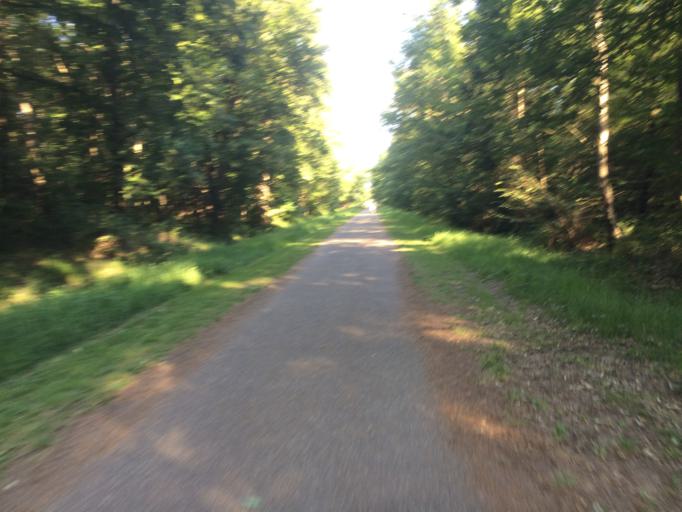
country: FR
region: Ile-de-France
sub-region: Departement du Val-de-Marne
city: Boissy-Saint-Leger
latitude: 48.7458
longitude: 2.5175
